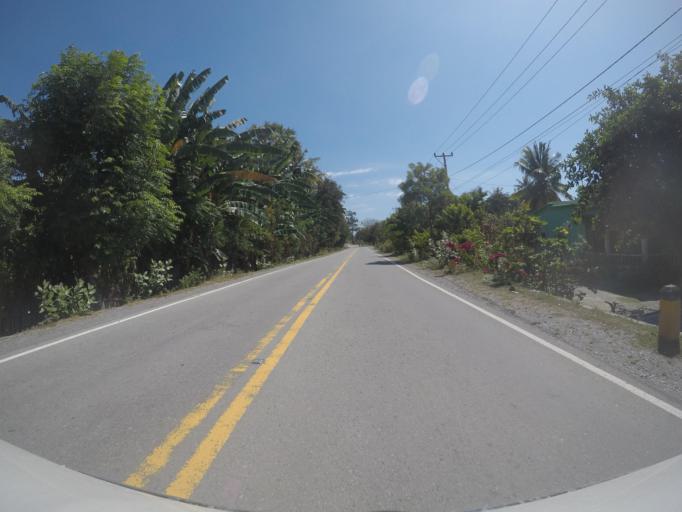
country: TL
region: Liquica
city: Liquica
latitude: -8.5826
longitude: 125.3565
